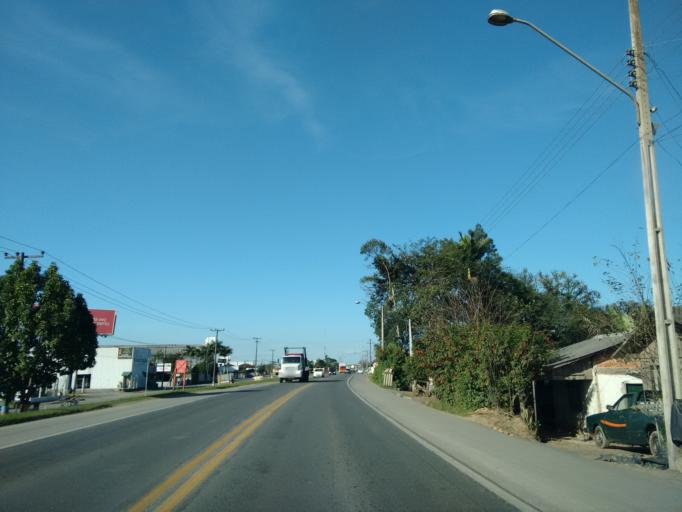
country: BR
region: Santa Catarina
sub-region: Guaramirim
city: Guaramirim
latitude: -26.4755
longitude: -48.9918
